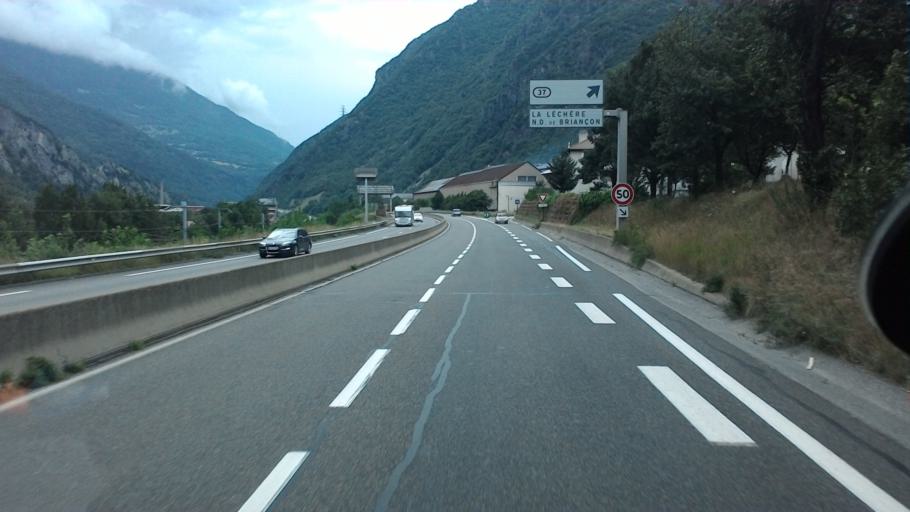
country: FR
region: Rhone-Alpes
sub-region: Departement de la Savoie
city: Aigueblanche
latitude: 45.5184
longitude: 6.4864
